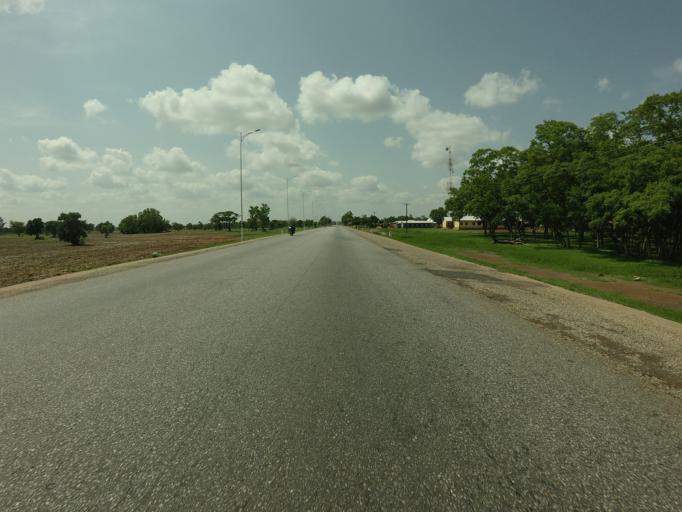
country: GH
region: Northern
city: Savelugu
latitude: 9.5444
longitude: -0.8385
